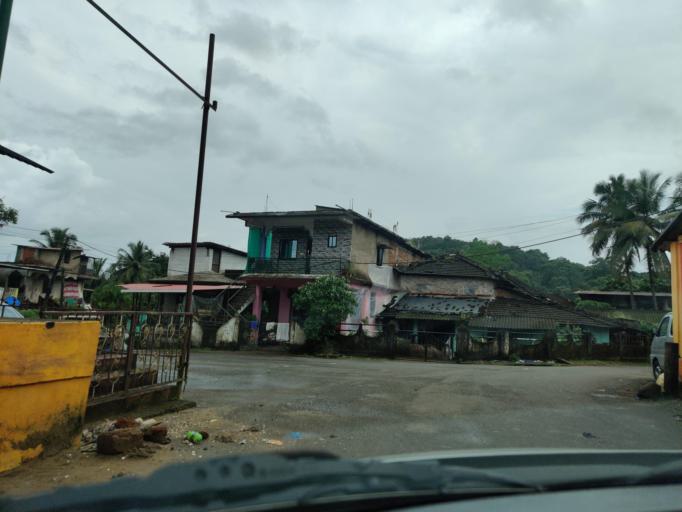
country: IN
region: Goa
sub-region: North Goa
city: Valpoy
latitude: 15.5259
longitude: 74.1424
